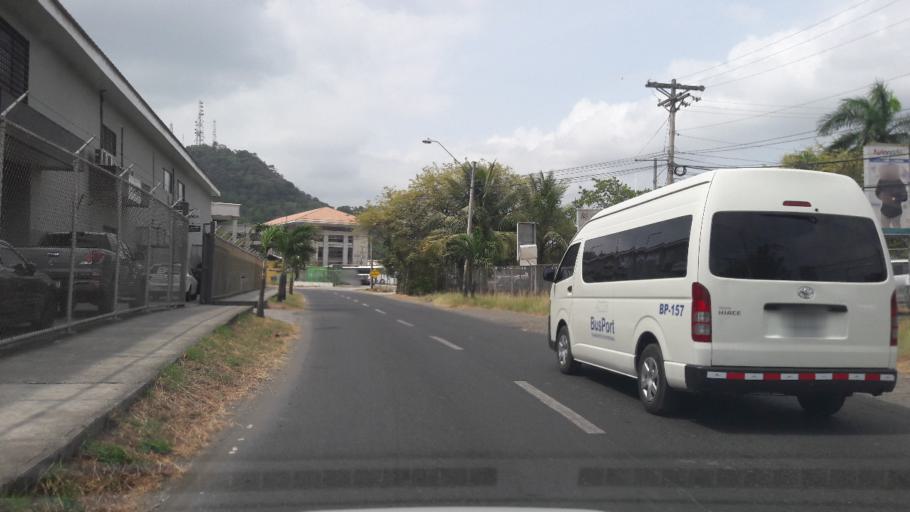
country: PA
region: Panama
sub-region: Distrito de Panama
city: Ancon
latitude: 8.9698
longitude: -79.5479
